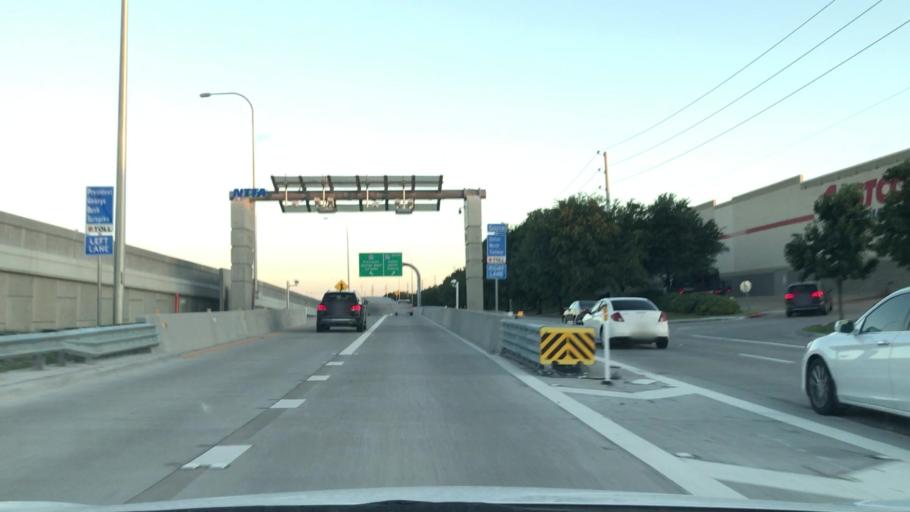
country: US
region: Texas
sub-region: Dallas County
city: Addison
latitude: 33.0255
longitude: -96.8302
